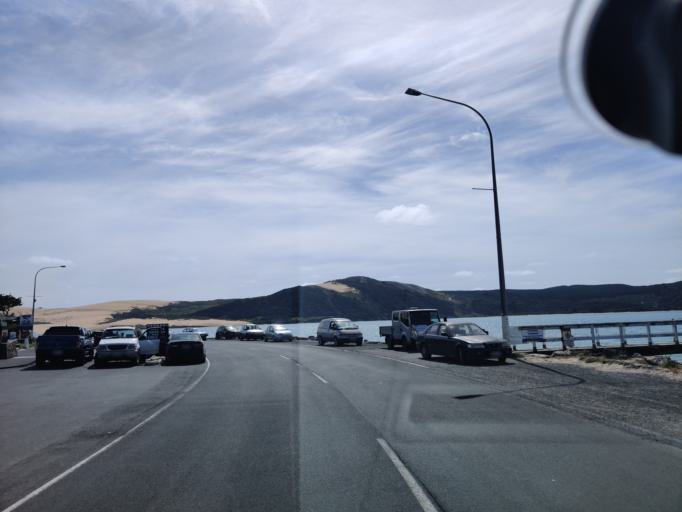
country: NZ
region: Northland
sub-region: Far North District
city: Ahipara
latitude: -35.5045
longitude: 173.3923
